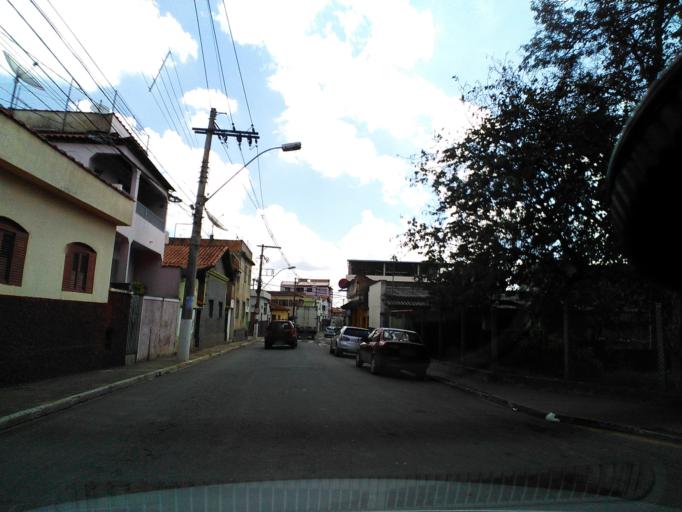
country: BR
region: Minas Gerais
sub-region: Tres Coracoes
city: Tres Coracoes
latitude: -21.7013
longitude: -45.2633
